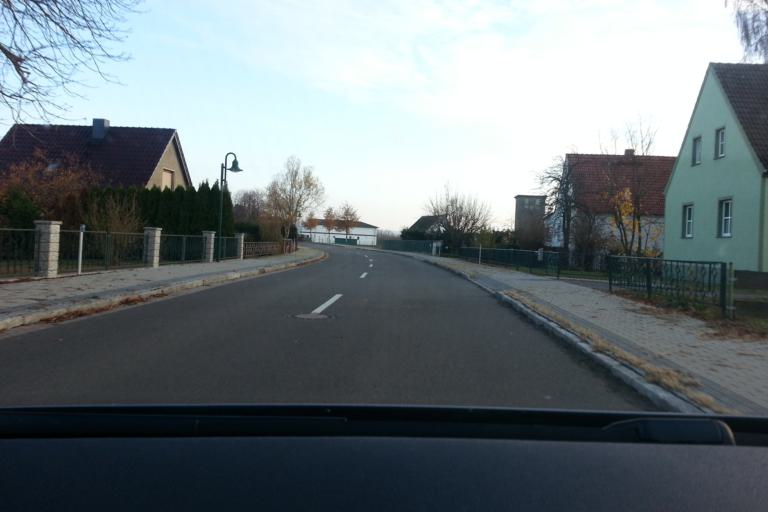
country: DE
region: Mecklenburg-Vorpommern
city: Strasburg
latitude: 53.6171
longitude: 13.7680
